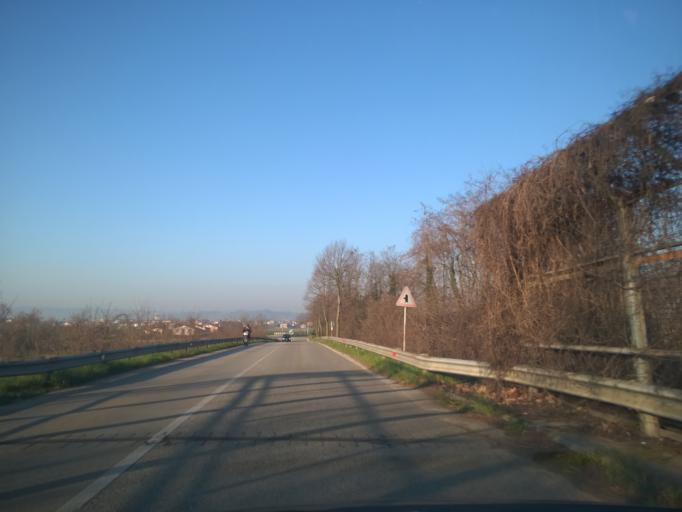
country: IT
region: Veneto
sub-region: Provincia di Vicenza
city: Villaggio Montegrappa
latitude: 45.5524
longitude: 11.6155
